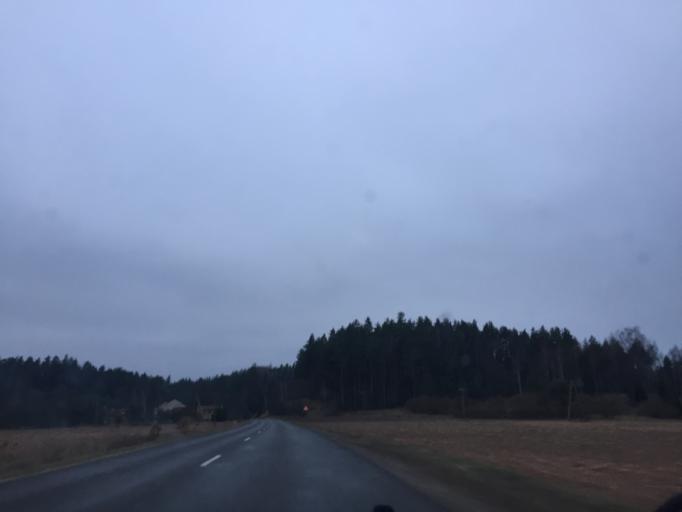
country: LV
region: Priekuli
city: Priekuli
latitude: 57.3302
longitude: 25.3997
